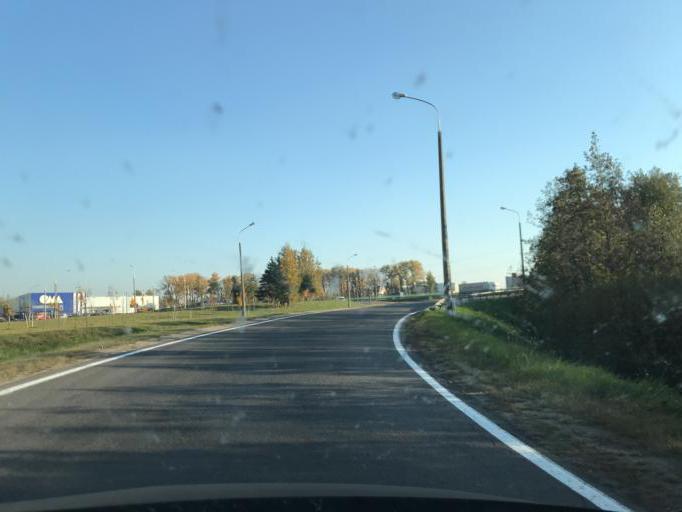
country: BY
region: Minsk
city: Shchomyslitsa
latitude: 53.8436
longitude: 27.4721
